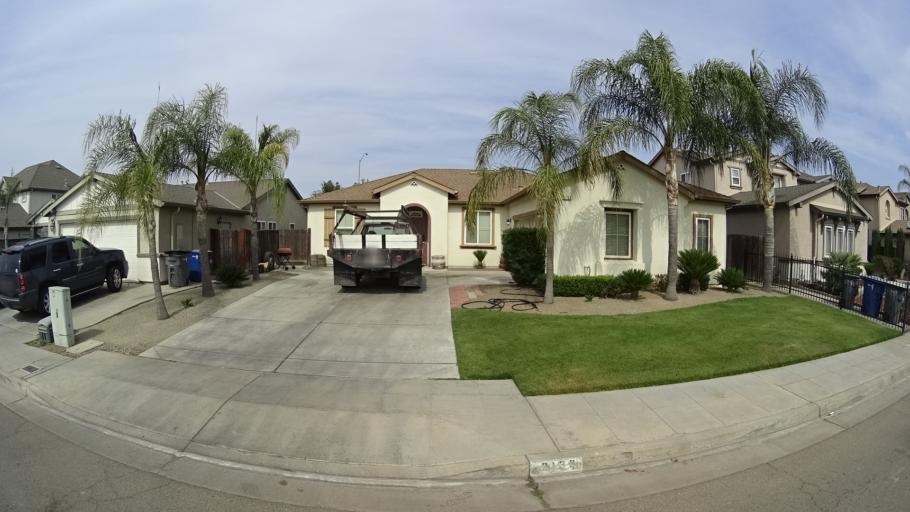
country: US
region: California
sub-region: Fresno County
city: West Park
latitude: 36.7673
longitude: -119.8886
